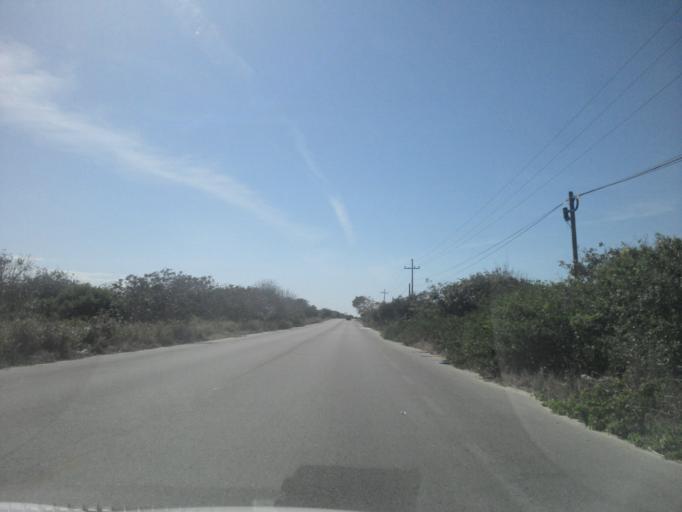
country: MX
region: Yucatan
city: Telchac Puerto
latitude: 21.3297
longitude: -89.3815
